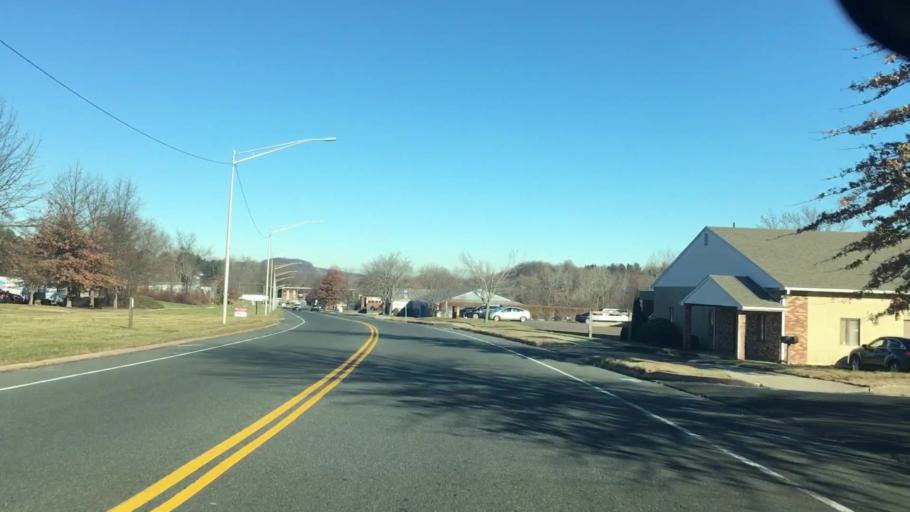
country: US
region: Connecticut
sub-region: New Haven County
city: Meriden
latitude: 41.5213
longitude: -72.7601
